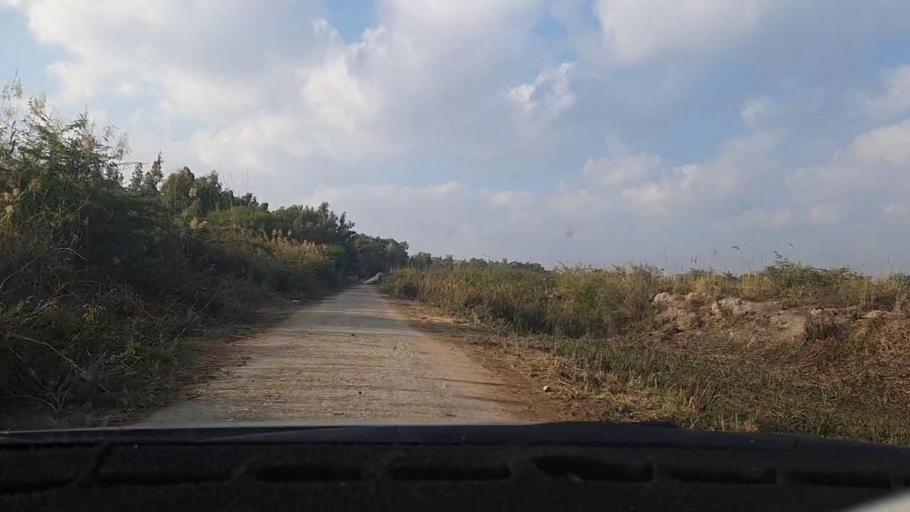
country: PK
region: Sindh
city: Tando Mittha Khan
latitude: 25.9110
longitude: 69.3046
